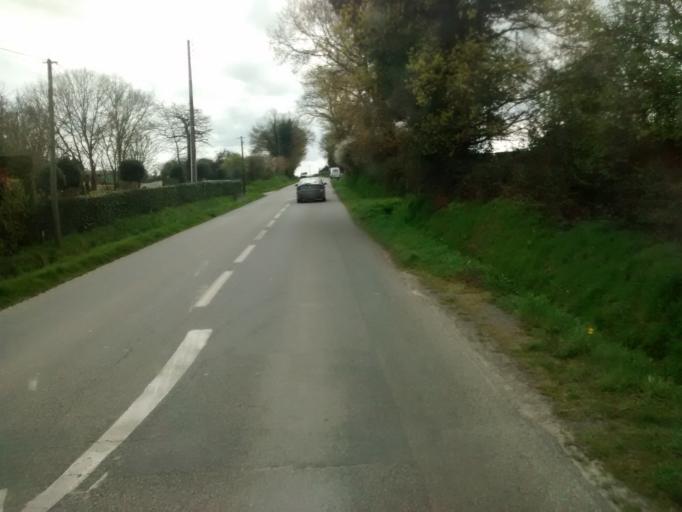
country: FR
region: Brittany
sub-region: Departement du Morbihan
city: Ploermel
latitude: 47.9098
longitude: -2.3864
